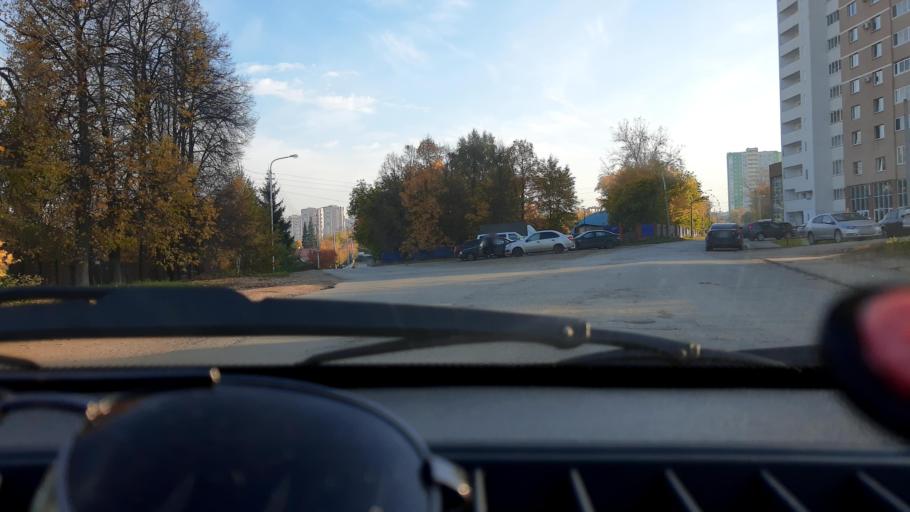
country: RU
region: Bashkortostan
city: Ufa
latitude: 54.7083
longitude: 55.9778
